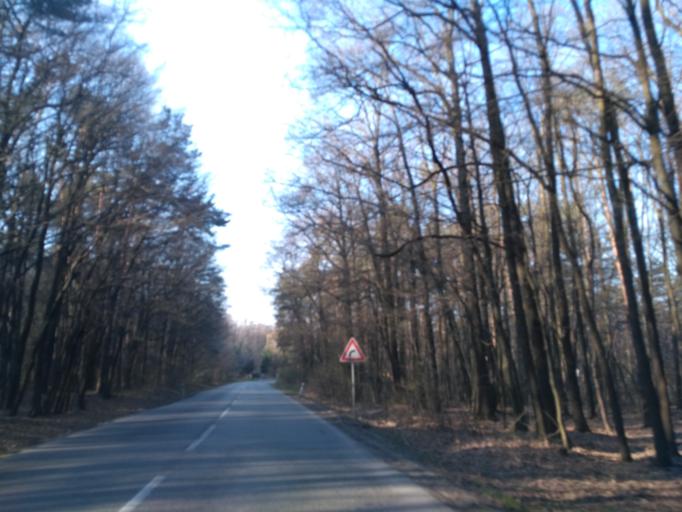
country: SK
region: Kosicky
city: Kosice
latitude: 48.6746
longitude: 21.1749
